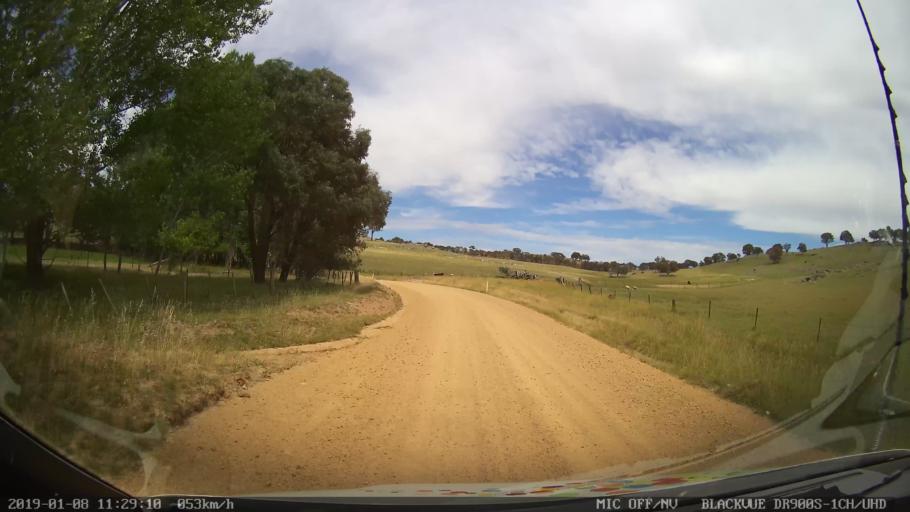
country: AU
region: New South Wales
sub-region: Guyra
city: Guyra
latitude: -30.2992
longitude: 151.5492
